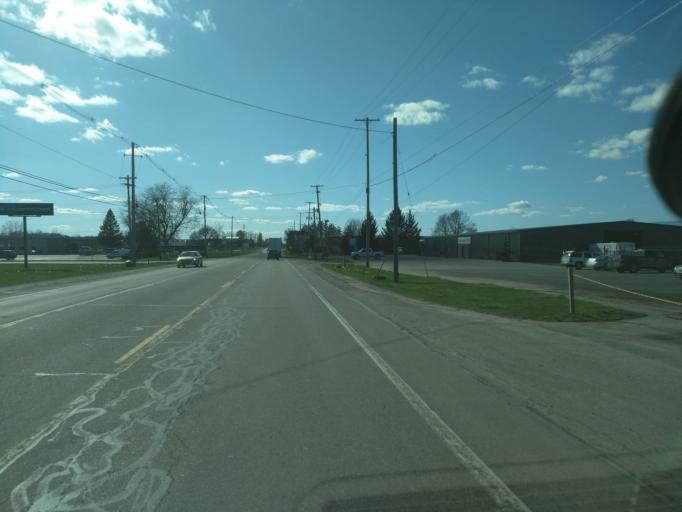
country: US
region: Michigan
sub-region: Eaton County
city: Waverly
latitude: 42.7759
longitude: -84.6231
